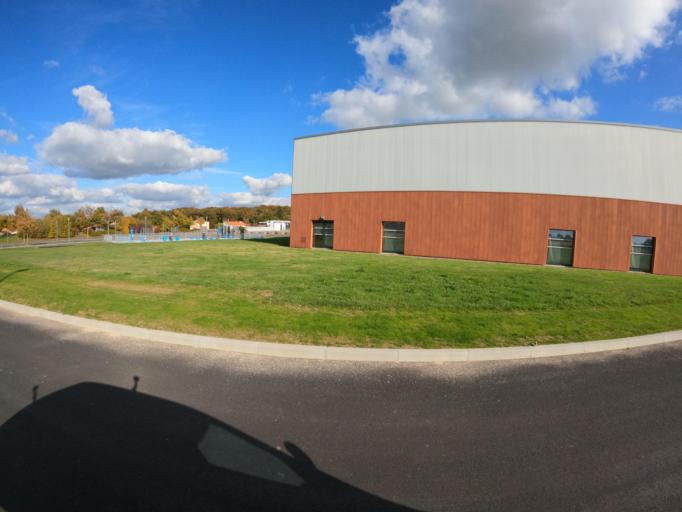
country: FR
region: Pays de la Loire
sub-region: Departement de la Loire-Atlantique
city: Aigrefeuille-sur-Maine
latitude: 47.0745
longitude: -1.4157
